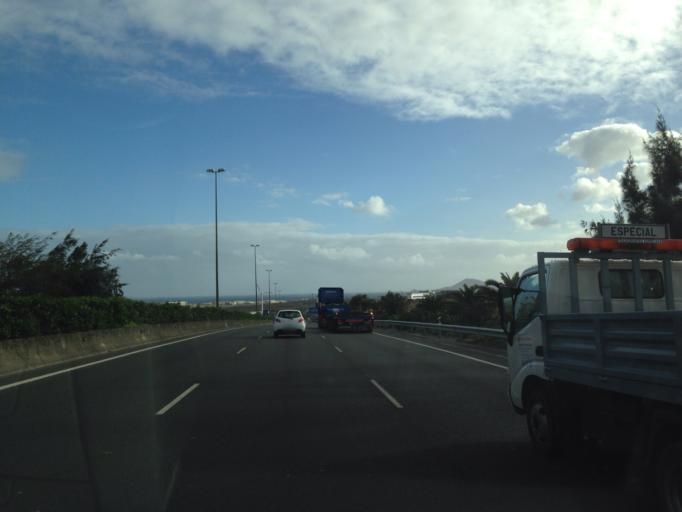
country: ES
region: Canary Islands
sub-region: Provincia de Las Palmas
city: Telde
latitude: 27.9586
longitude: -15.3886
